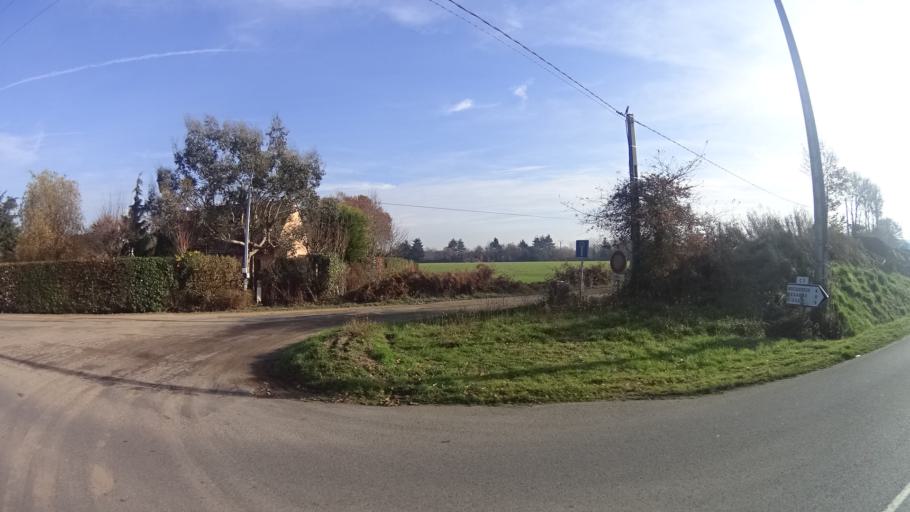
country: FR
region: Brittany
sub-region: Departement du Morbihan
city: Allaire
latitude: 47.6308
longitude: -2.1638
